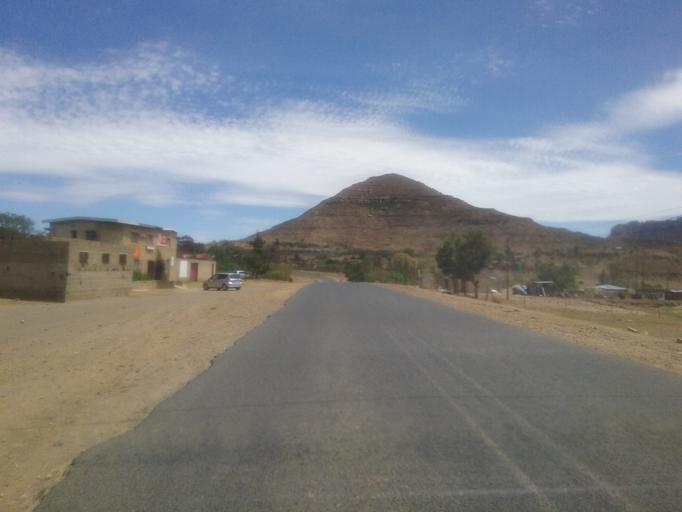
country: LS
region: Mafeteng
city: Mafeteng
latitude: -29.9571
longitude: 27.2889
